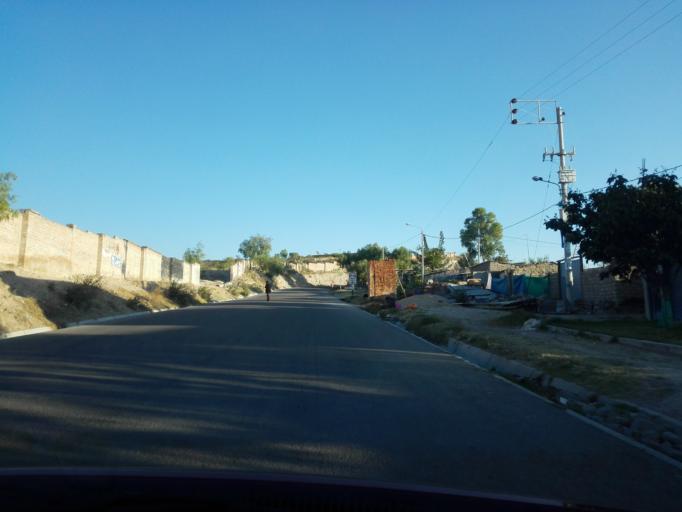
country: PE
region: Ayacucho
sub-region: Provincia de Huamanga
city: Ayacucho
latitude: -13.1420
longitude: -74.2220
